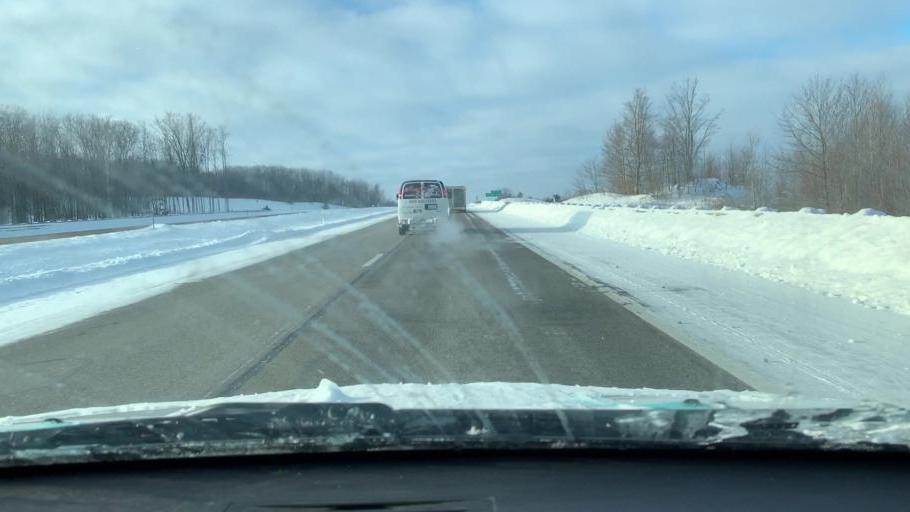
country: US
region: Michigan
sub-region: Wexford County
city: Cadillac
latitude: 44.2270
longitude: -85.3860
